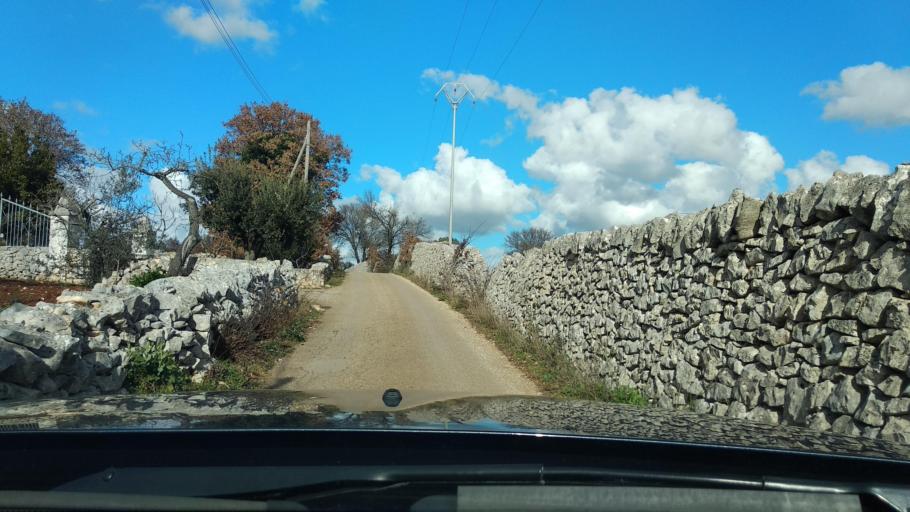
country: IT
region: Apulia
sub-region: Provincia di Brindisi
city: Casalini
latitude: 40.7088
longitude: 17.4534
